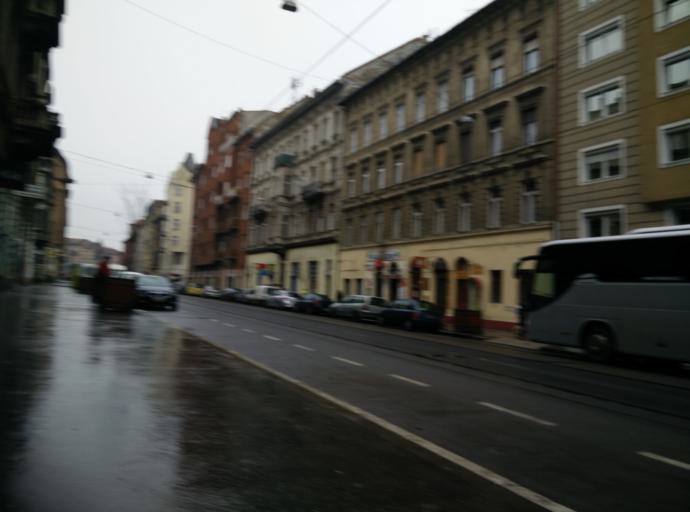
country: HU
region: Budapest
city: Budapest VIII. keruelet
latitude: 47.4944
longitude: 19.0785
